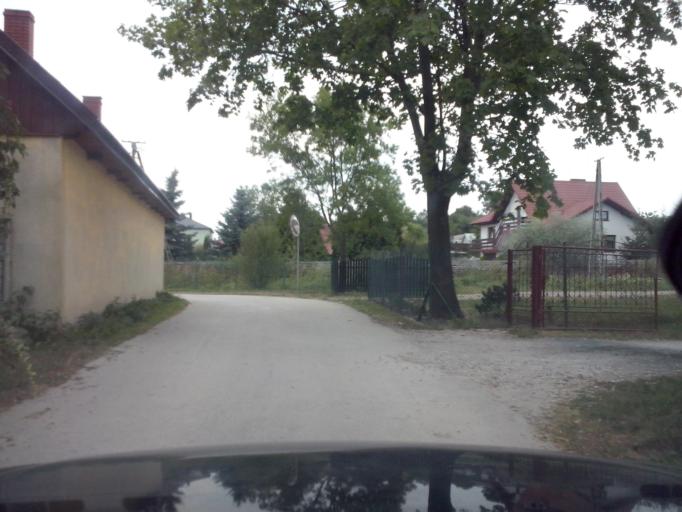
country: PL
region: Swietokrzyskie
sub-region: Powiat kielecki
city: Morawica
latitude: 50.6815
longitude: 20.6056
